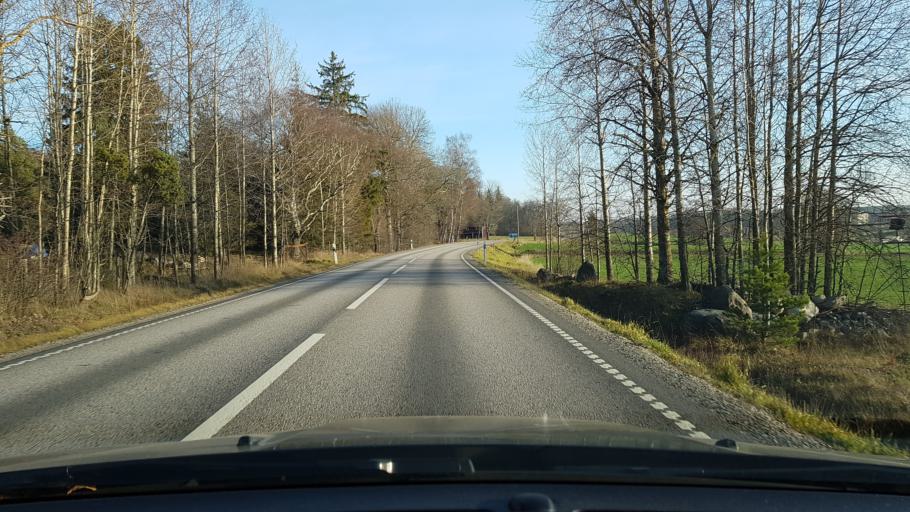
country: SE
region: Stockholm
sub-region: Norrtalje Kommun
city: Nykvarn
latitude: 59.7400
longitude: 18.1735
